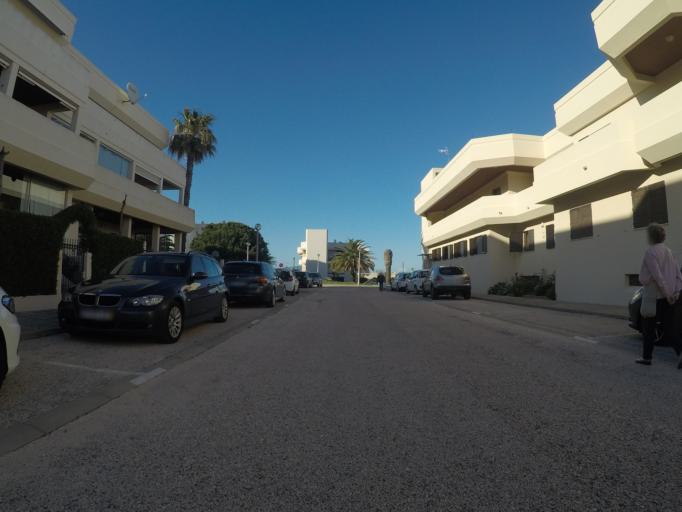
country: PT
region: Faro
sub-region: Lagos
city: Lagos
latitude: 37.0924
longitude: -8.6703
